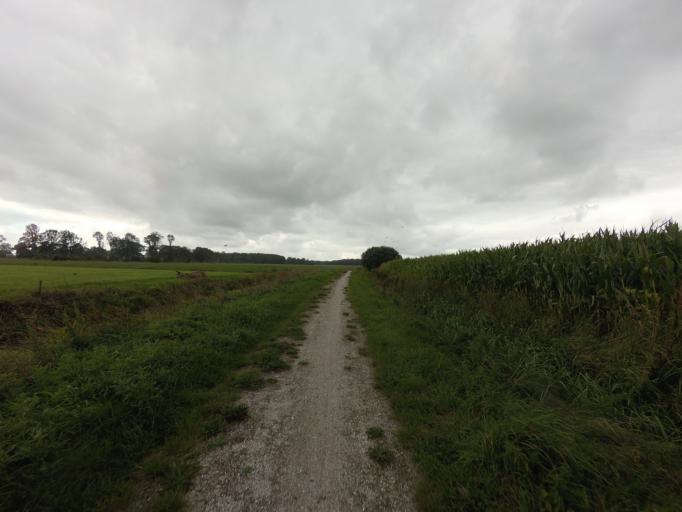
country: NL
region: Friesland
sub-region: Gemeente Weststellingwerf
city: Noordwolde
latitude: 52.9391
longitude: 6.1884
